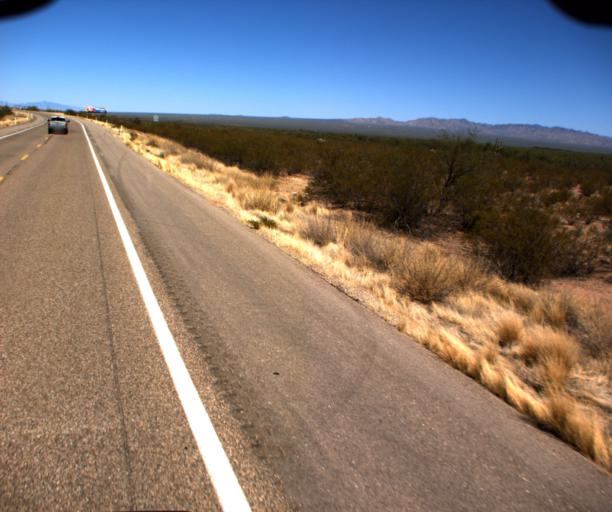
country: US
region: Arizona
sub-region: Pima County
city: Three Points
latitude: 32.0415
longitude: -111.4469
